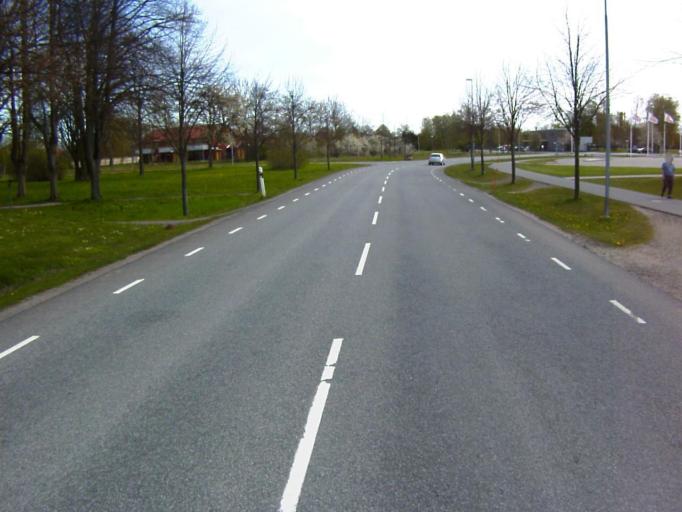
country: SE
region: Skane
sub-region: Kristianstads Kommun
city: Kristianstad
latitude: 56.0442
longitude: 14.1485
